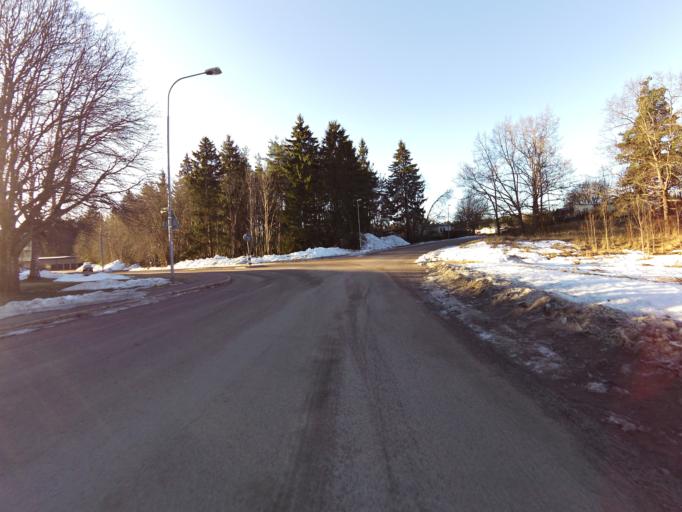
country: SE
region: Gaevleborg
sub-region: Gavle Kommun
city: Gavle
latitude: 60.6587
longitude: 17.1488
